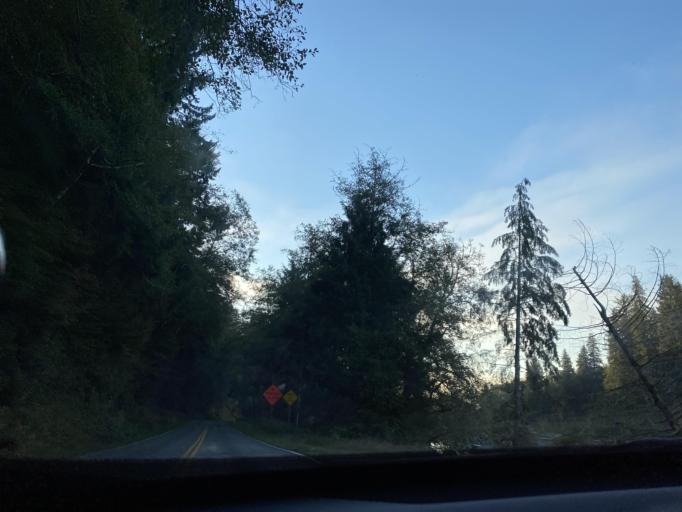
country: US
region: Washington
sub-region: Clallam County
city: Forks
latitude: 47.8232
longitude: -124.1870
